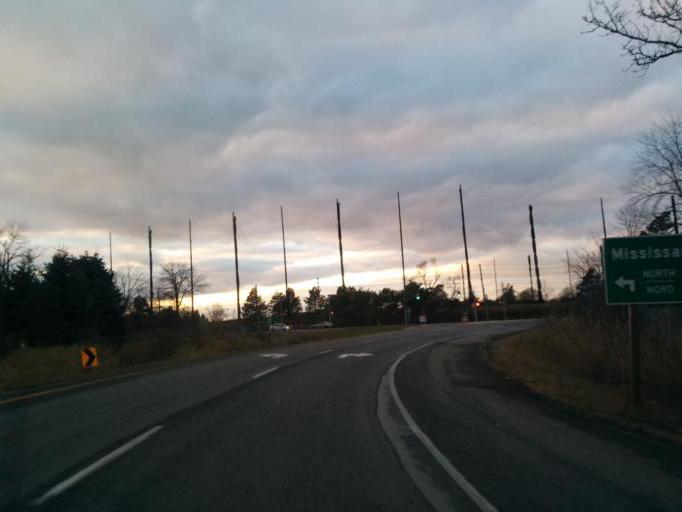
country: CA
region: Ontario
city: Mississauga
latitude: 43.5508
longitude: -79.6172
